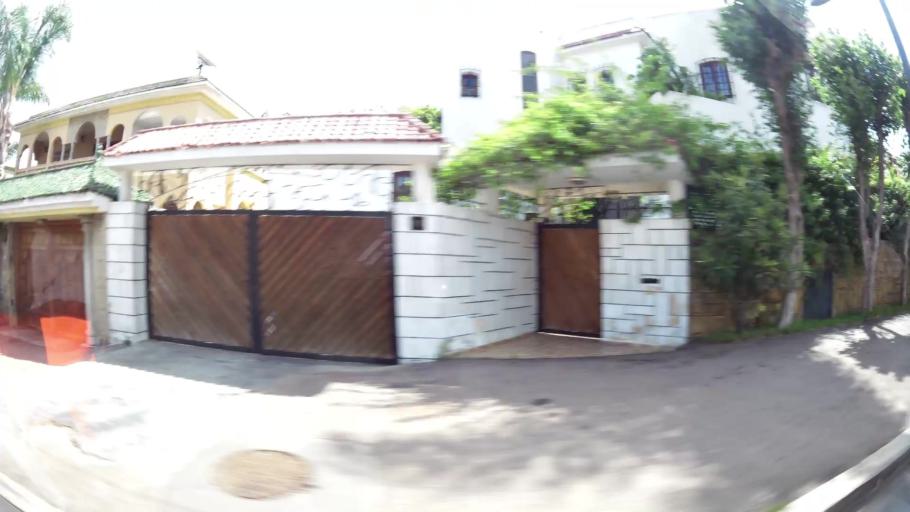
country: MA
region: Grand Casablanca
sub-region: Casablanca
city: Casablanca
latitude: 33.5492
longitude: -7.6319
